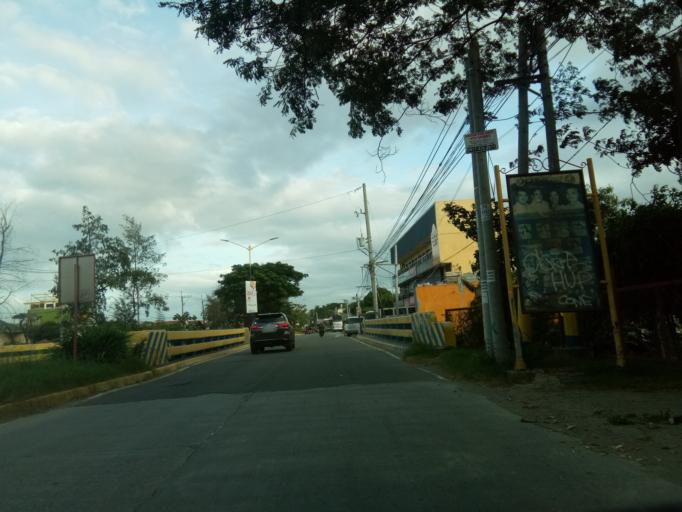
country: PH
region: Calabarzon
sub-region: Province of Cavite
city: Imus
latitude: 14.3873
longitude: 120.9724
